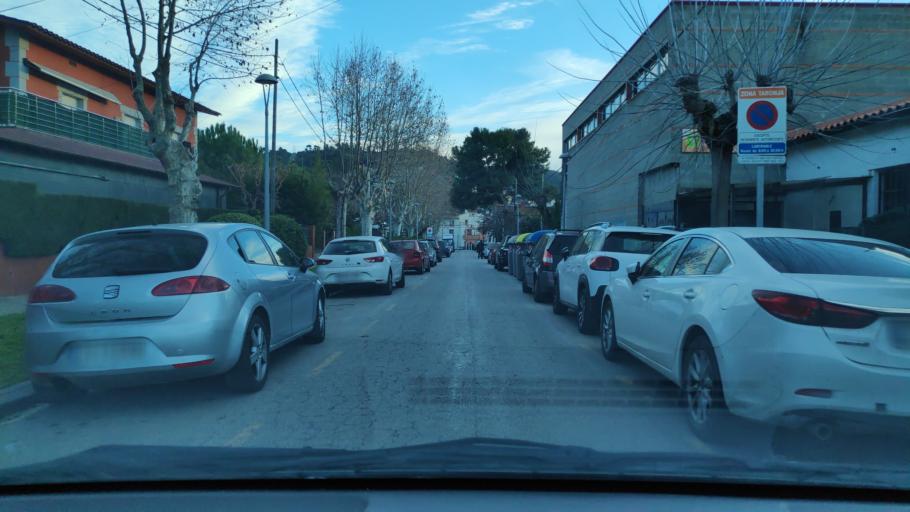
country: ES
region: Catalonia
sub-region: Provincia de Barcelona
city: Montmelo
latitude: 41.5494
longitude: 2.2488
